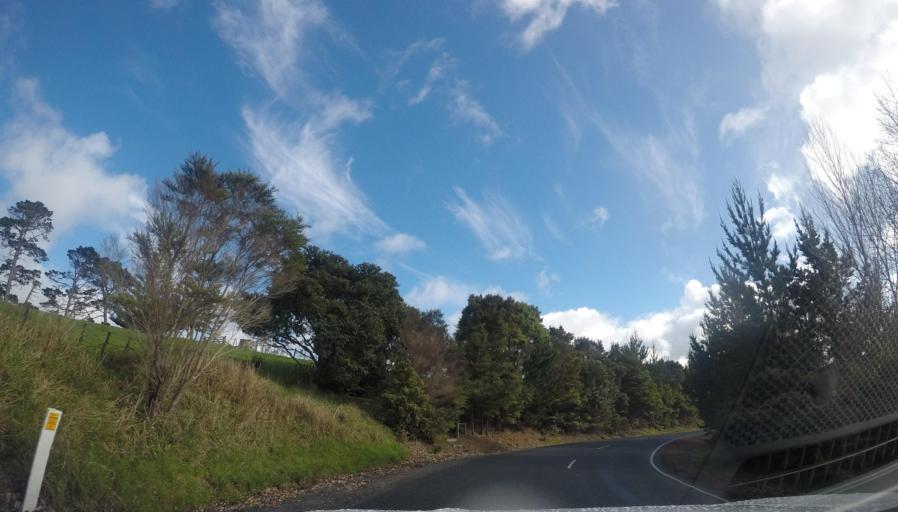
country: NZ
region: Auckland
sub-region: Auckland
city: Warkworth
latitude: -36.4592
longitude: 174.7322
